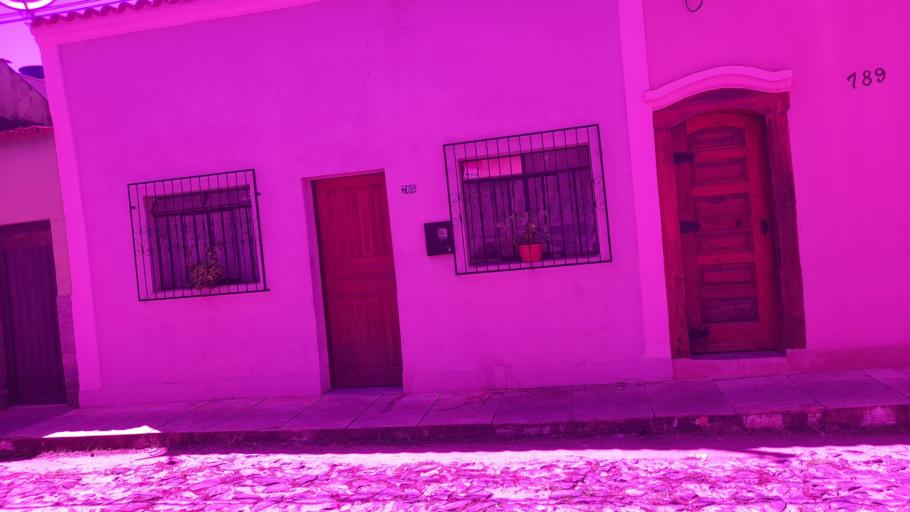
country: BR
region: Minas Gerais
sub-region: Sao Joao Del Rei
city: Sao Joao del Rei
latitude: -21.1387
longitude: -44.2700
